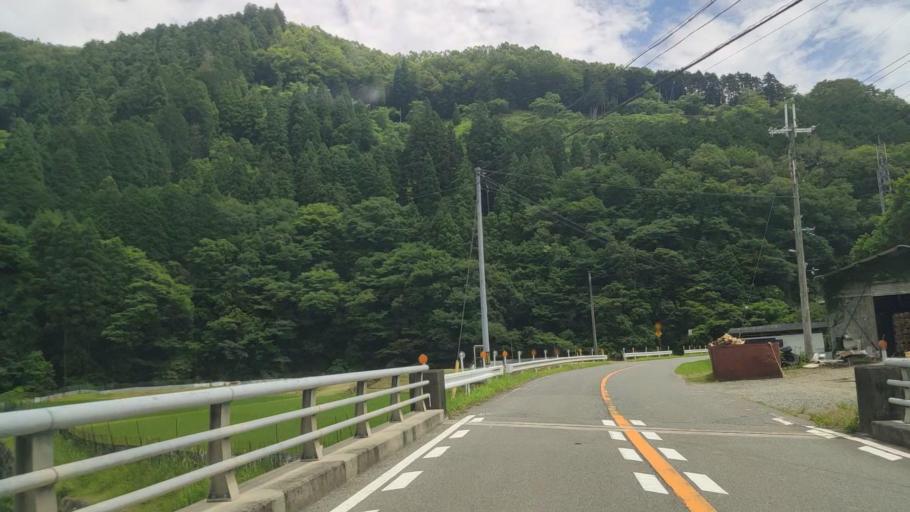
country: JP
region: Hyogo
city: Yamazakicho-nakabirose
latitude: 35.0798
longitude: 134.3601
